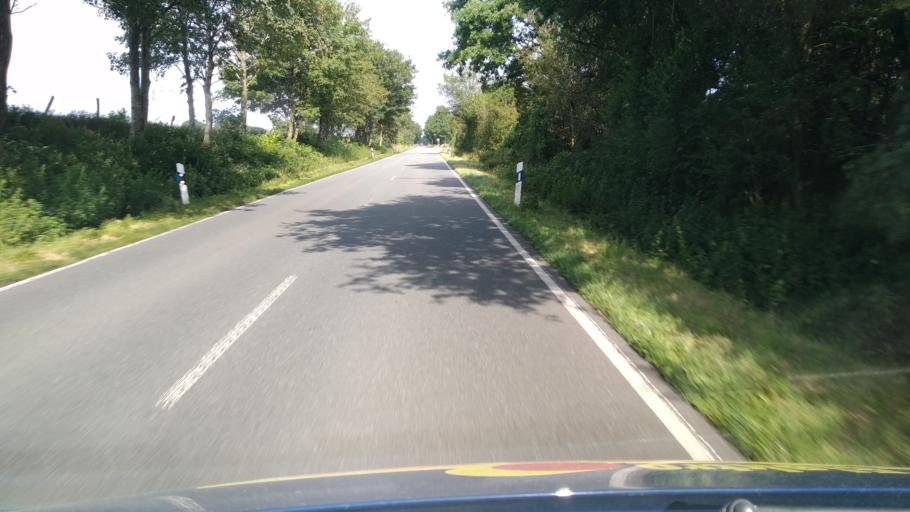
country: DE
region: Schleswig-Holstein
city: Geltorf
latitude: 54.4369
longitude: 9.6038
